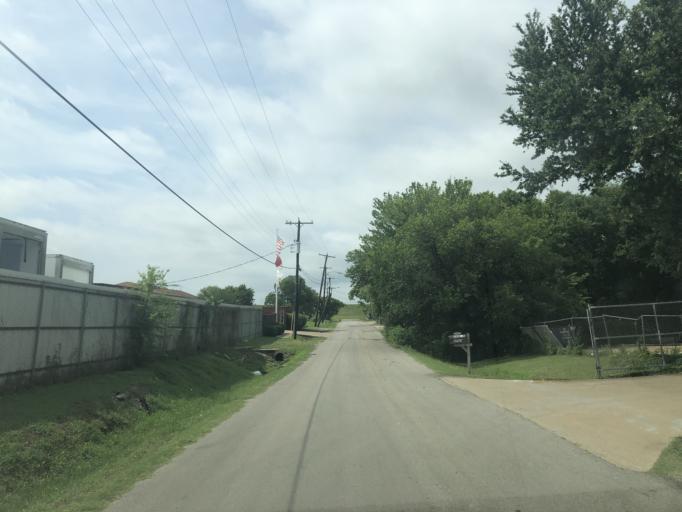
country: US
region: Texas
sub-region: Dallas County
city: Cockrell Hill
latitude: 32.8049
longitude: -96.8752
